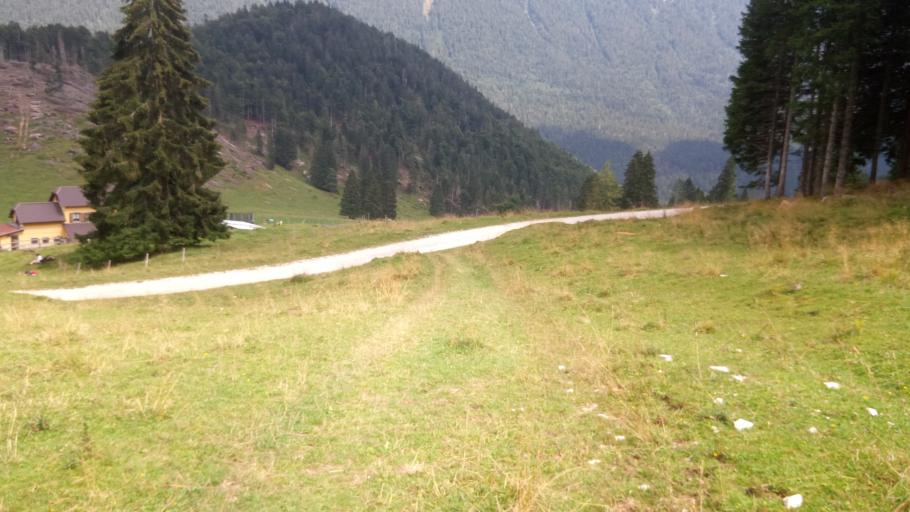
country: IT
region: Veneto
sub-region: Provincia di Vicenza
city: Roana
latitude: 45.9433
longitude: 11.4189
